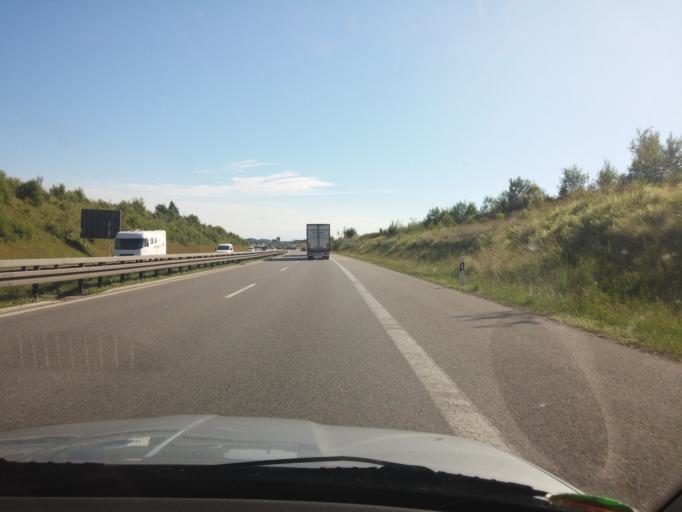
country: DE
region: Baden-Wuerttemberg
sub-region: Tuebingen Region
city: Kisslegg
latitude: 47.7594
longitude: 9.9132
